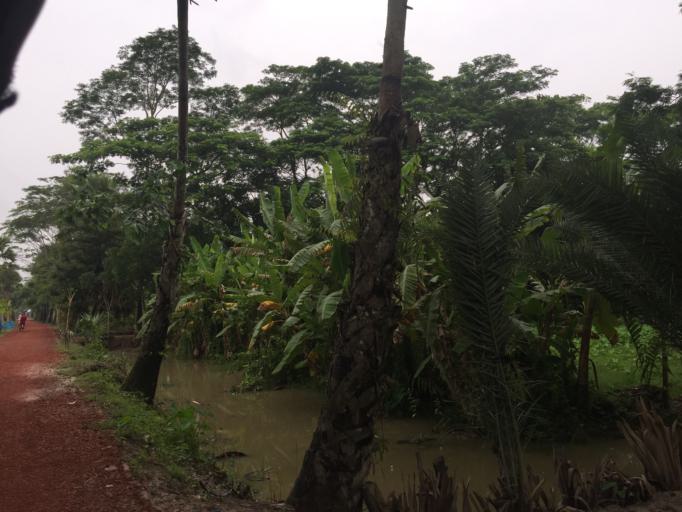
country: BD
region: Barisal
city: Mathba
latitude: 22.2057
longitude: 89.9375
